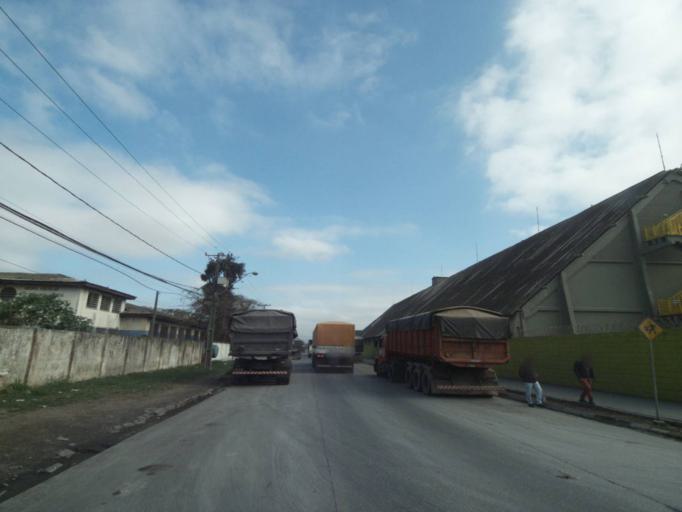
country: BR
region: Parana
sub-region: Paranagua
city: Paranagua
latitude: -25.5107
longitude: -48.5215
